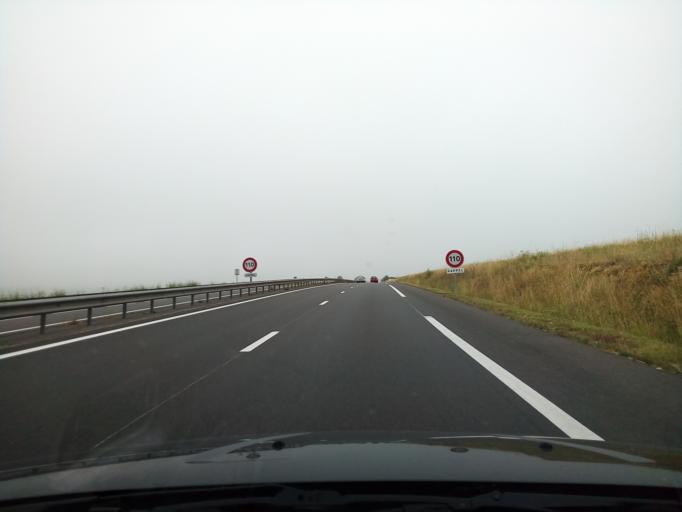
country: FR
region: Poitou-Charentes
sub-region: Departement de la Charente
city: Gensac-la-Pallue
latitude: 45.6660
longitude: -0.2405
